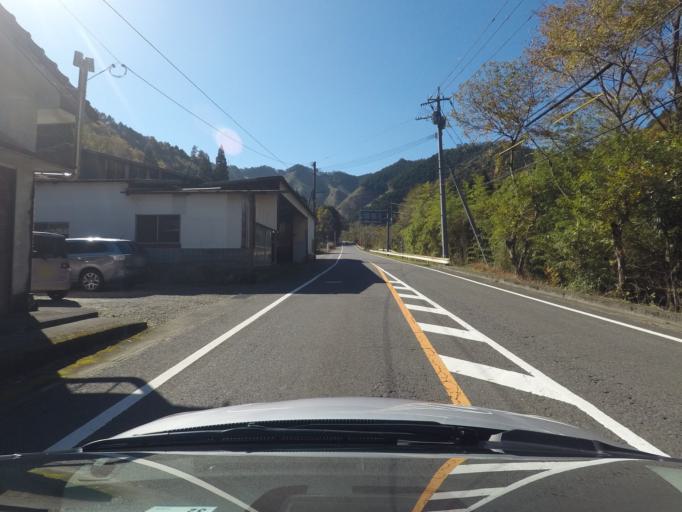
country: JP
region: Miyazaki
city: Kobayashi
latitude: 32.0604
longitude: 131.0782
